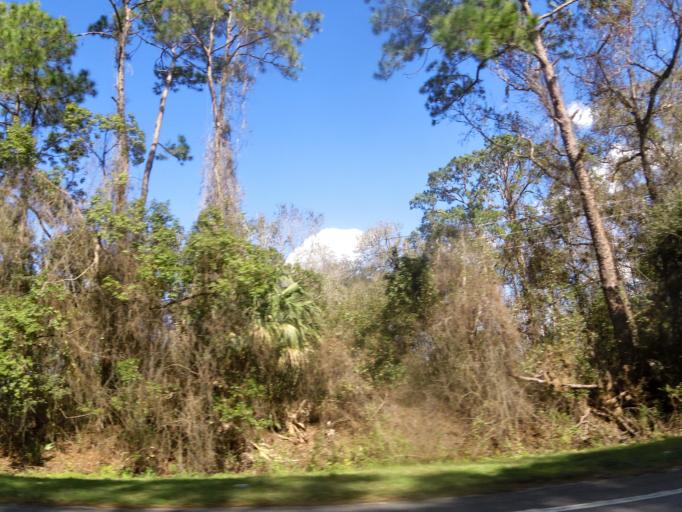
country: US
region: Florida
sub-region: Volusia County
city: De Leon Springs
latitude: 29.1557
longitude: -81.3807
